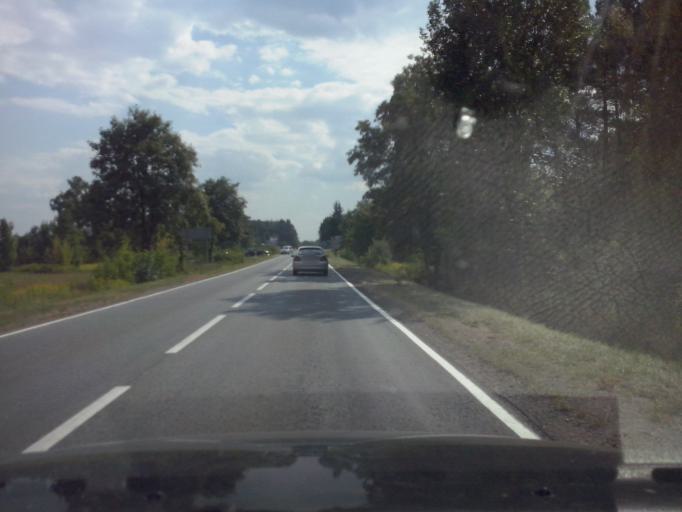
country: PL
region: Subcarpathian Voivodeship
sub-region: Powiat nizanski
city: Rudnik nad Sanem
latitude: 50.4620
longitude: 22.2429
